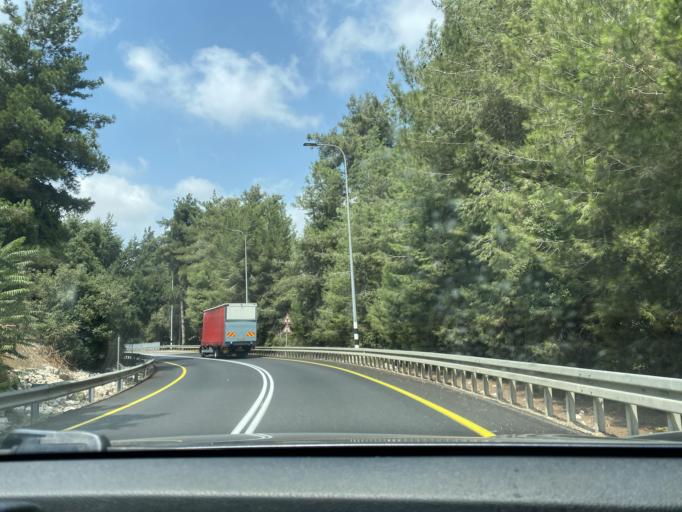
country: IL
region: Northern District
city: Kefar Weradim
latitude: 33.0039
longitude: 35.2842
